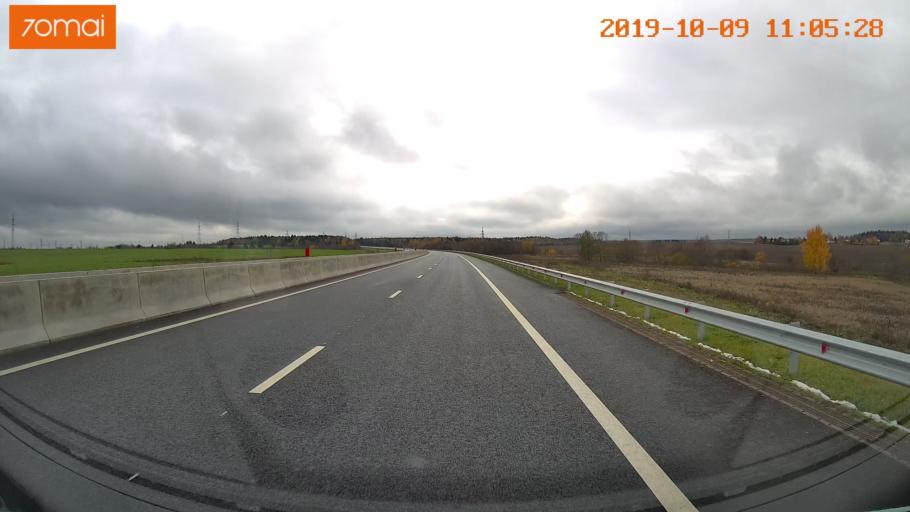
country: RU
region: Vologda
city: Molochnoye
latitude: 59.1994
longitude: 39.7577
